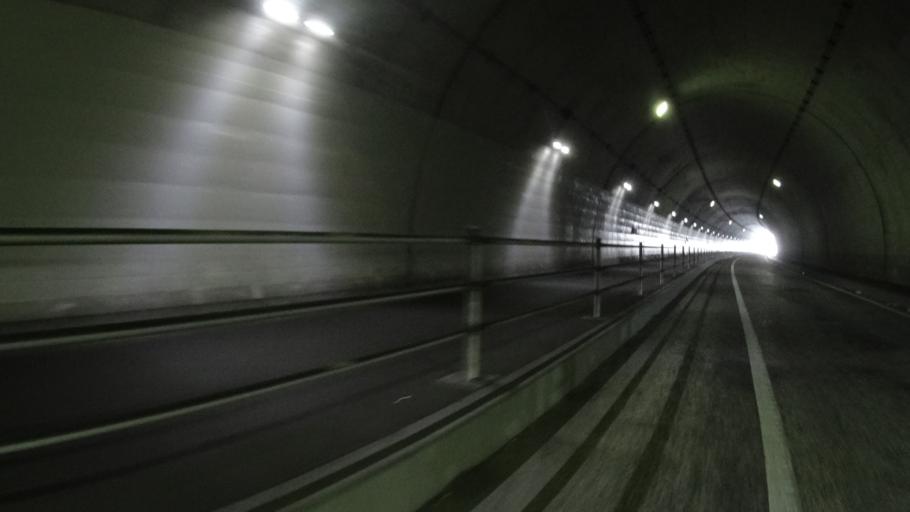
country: JP
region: Kanagawa
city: Zushi
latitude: 35.2866
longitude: 139.5802
